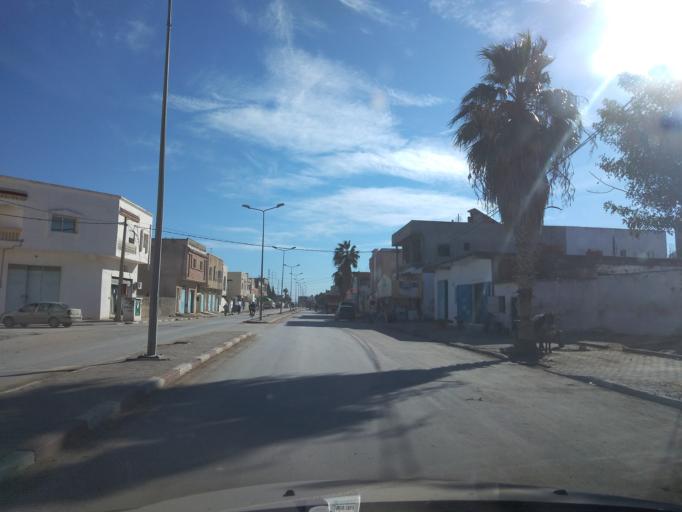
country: TN
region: Ariana
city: Qal'at al Andalus
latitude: 37.0596
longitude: 10.1193
